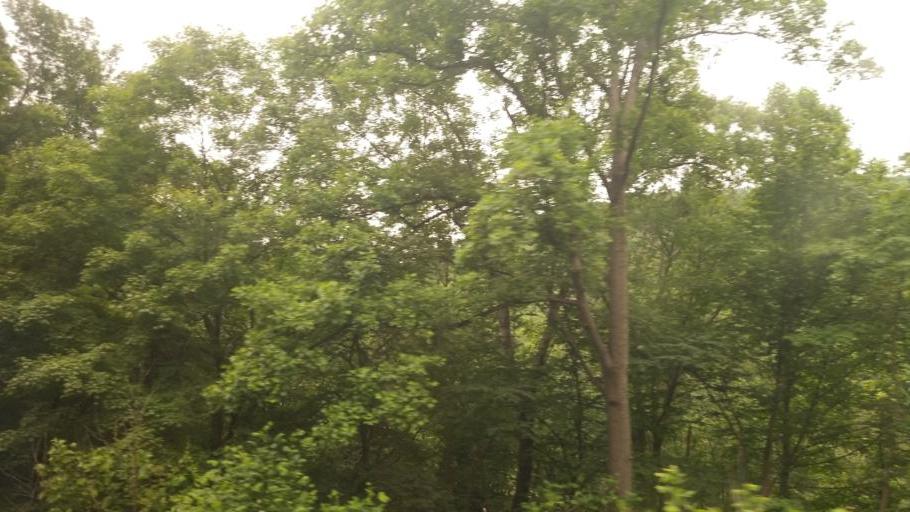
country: US
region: Pennsylvania
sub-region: Fayette County
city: South Connellsville
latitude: 39.9064
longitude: -79.4879
